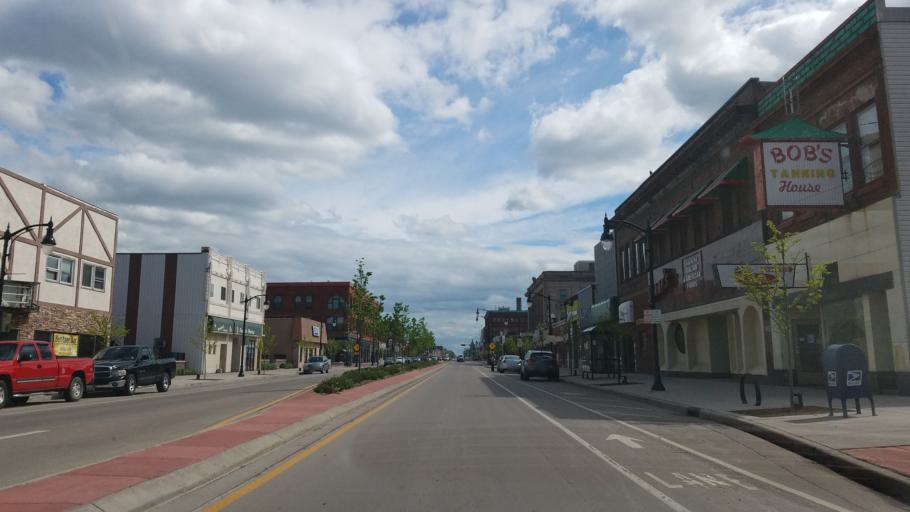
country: US
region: Wisconsin
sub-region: Douglas County
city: Superior
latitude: 46.7232
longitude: -92.1040
